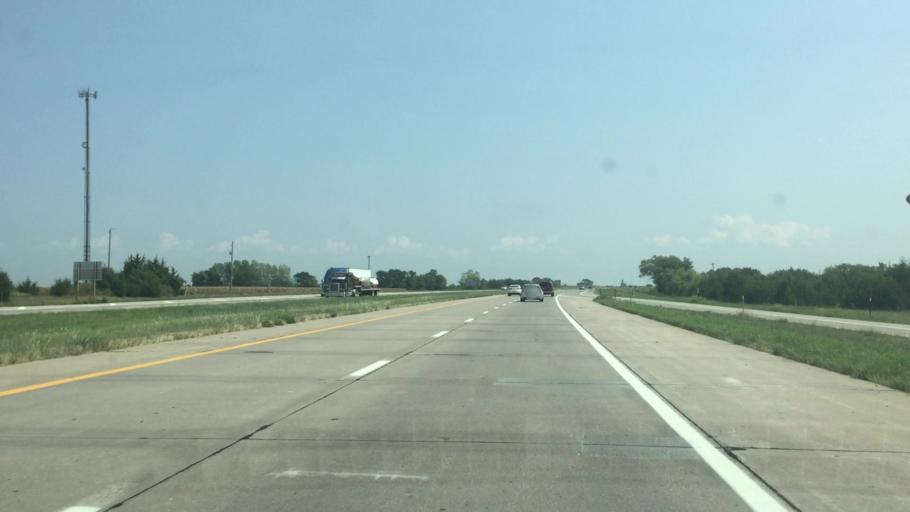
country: US
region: Kansas
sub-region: Franklin County
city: Ottawa
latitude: 38.4905
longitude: -95.4717
